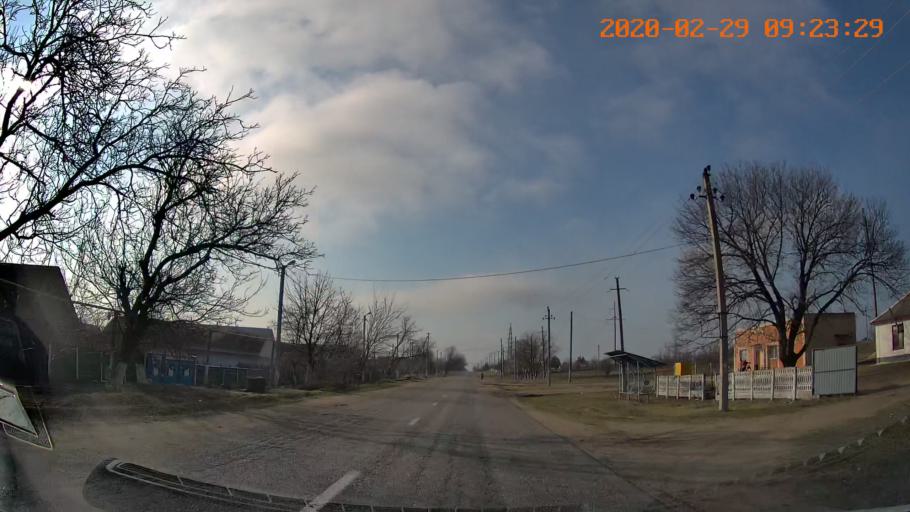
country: MD
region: Telenesti
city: Pervomaisc
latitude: 46.7253
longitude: 29.9611
